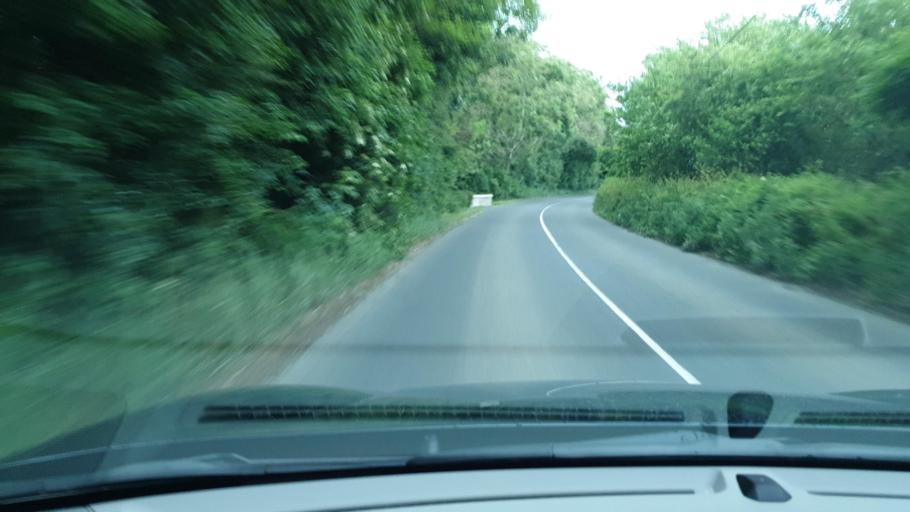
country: IE
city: Kentstown
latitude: 53.5932
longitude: -6.4998
